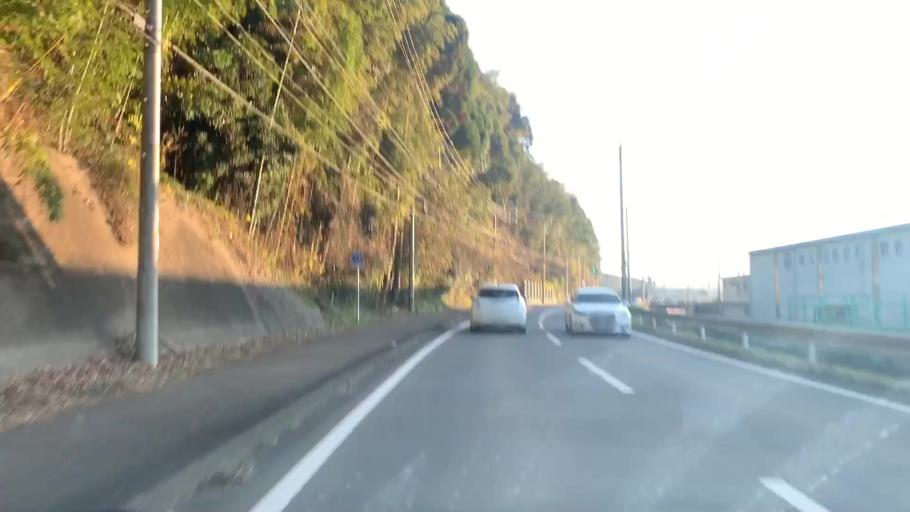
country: JP
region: Saga Prefecture
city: Imaricho-ko
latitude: 33.2883
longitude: 129.9709
